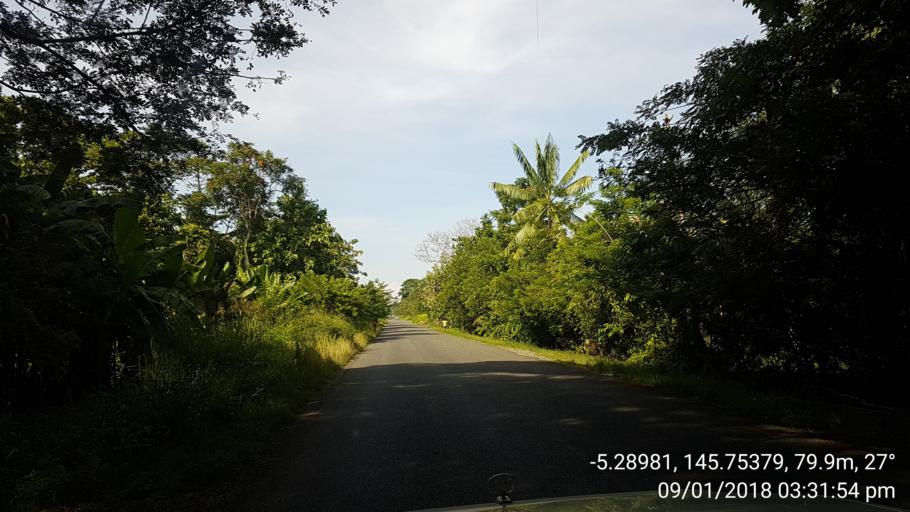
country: PG
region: Madang
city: Madang
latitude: -5.2900
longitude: 145.7536
